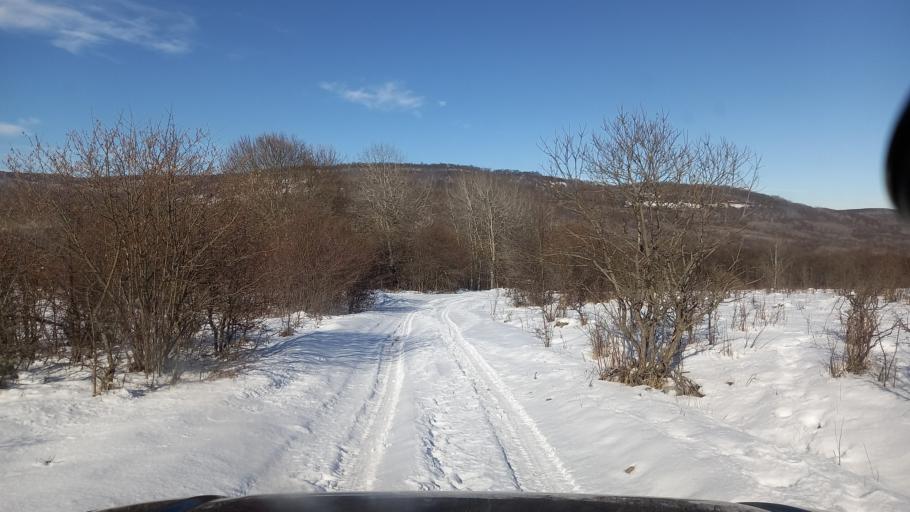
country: RU
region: Adygeya
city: Kamennomostskiy
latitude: 44.2362
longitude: 40.1505
